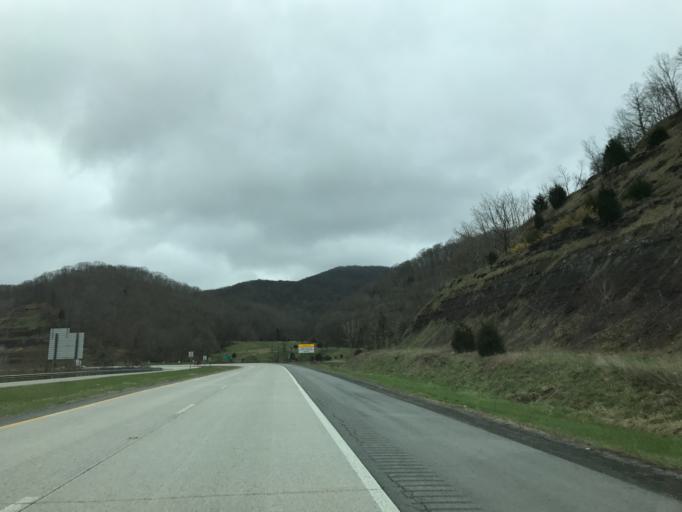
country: US
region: West Virginia
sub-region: Summers County
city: Hinton
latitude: 37.7856
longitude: -80.8832
